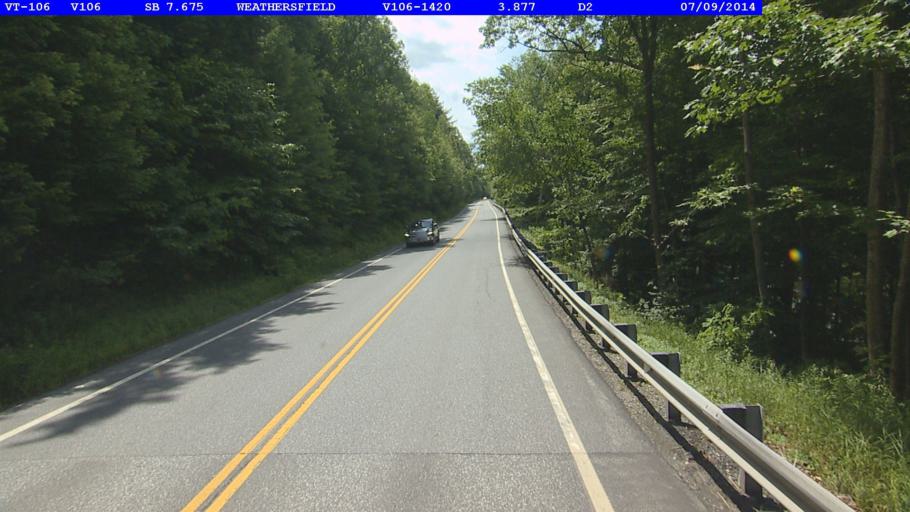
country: US
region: Vermont
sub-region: Windsor County
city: Springfield
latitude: 43.3942
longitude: -72.5138
